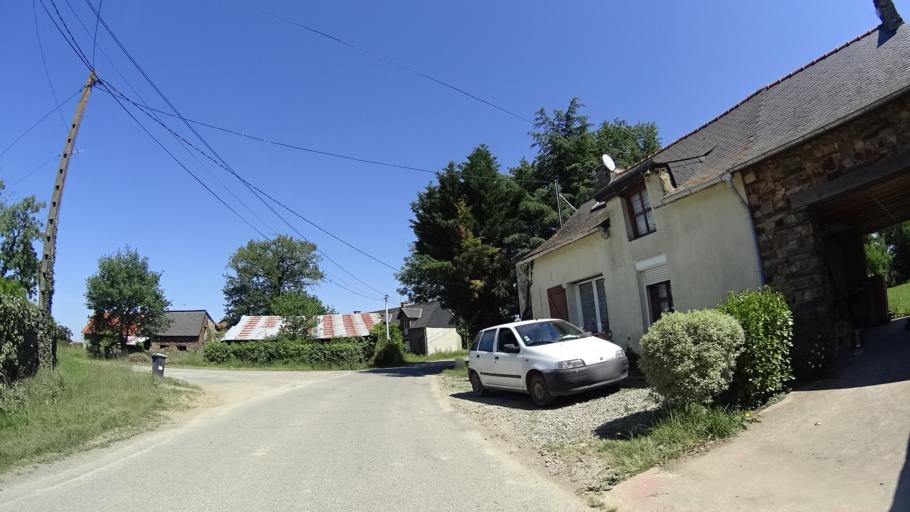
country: FR
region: Brittany
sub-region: Departement d'Ille-et-Vilaine
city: Messac
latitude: 47.7949
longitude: -1.8139
